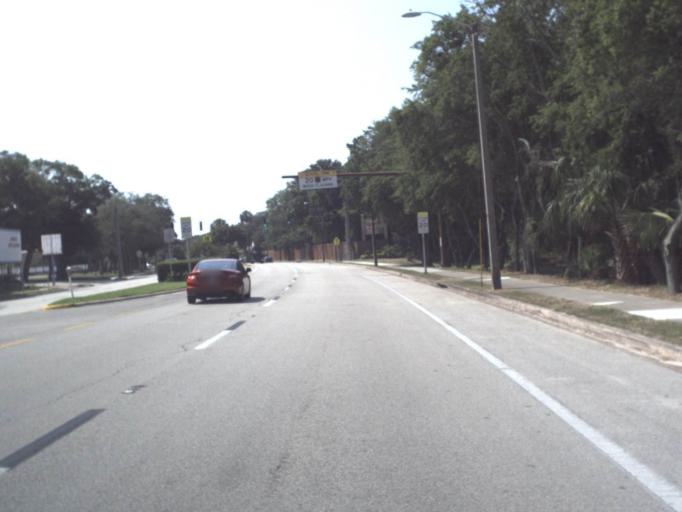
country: US
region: Florida
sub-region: Saint Johns County
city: Saint Augustine
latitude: 29.8844
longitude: -81.2903
